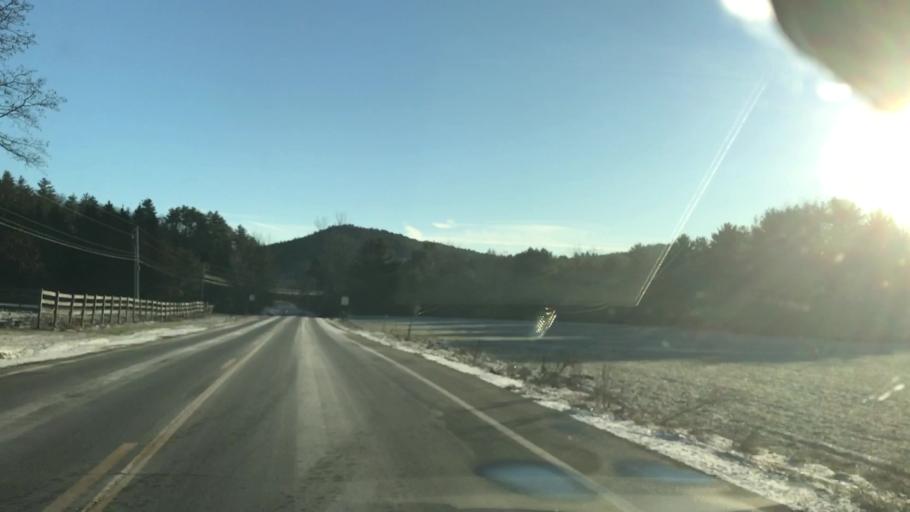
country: US
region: New Hampshire
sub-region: Grafton County
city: Lyme Town Offices
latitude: 43.8517
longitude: -72.1561
